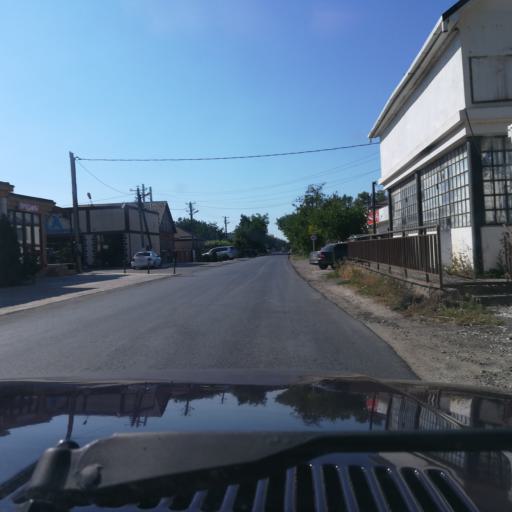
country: RU
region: Krasnodarskiy
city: Vityazevo
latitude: 45.0021
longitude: 37.2880
